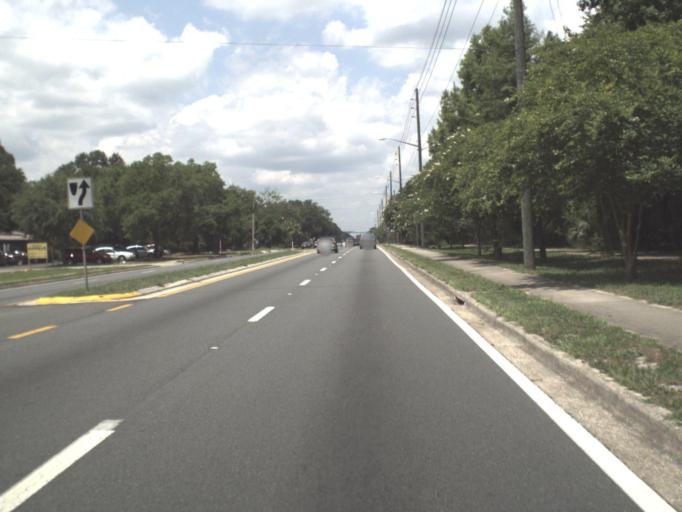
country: US
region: Florida
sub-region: Alachua County
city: Gainesville
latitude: 29.6555
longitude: -82.3090
